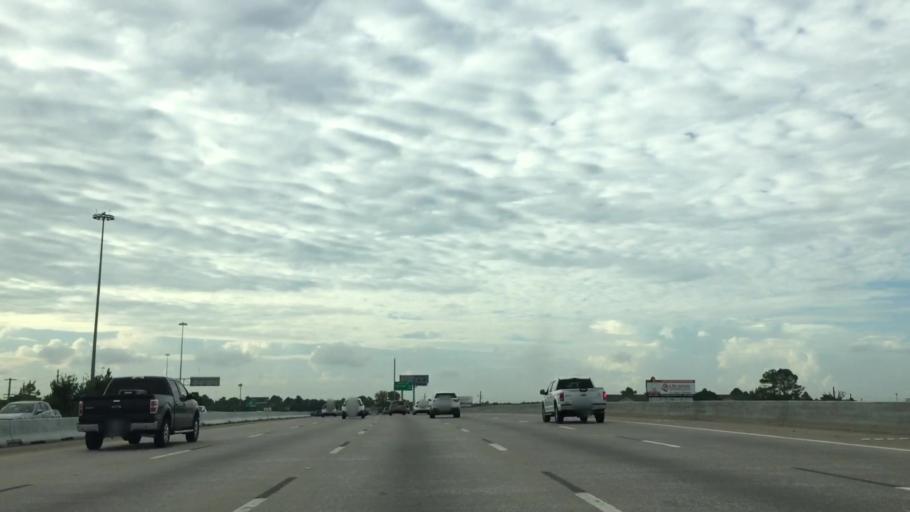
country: US
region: Texas
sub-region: Harris County
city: Oak Cliff Place
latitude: 29.9739
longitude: -95.5638
